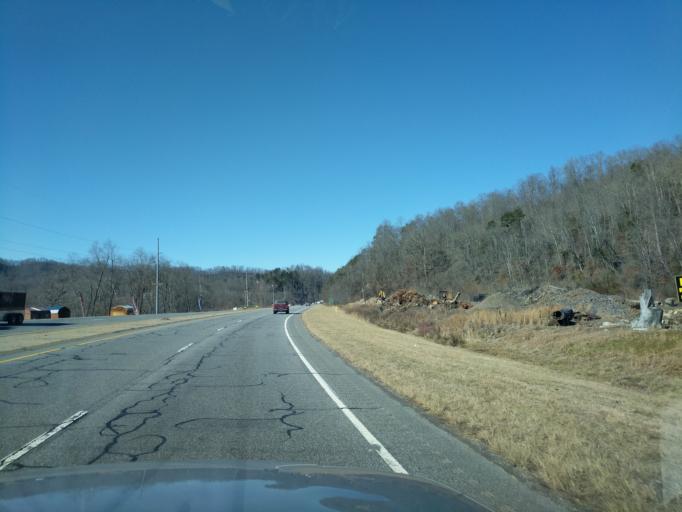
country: US
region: North Carolina
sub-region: Swain County
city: Cherokee
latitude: 35.4040
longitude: -83.3196
